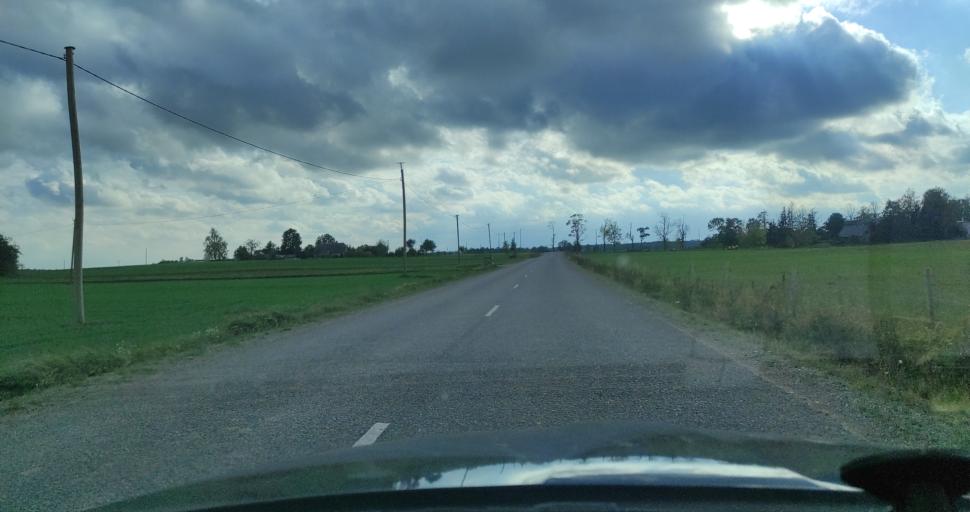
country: LV
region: Talsu Rajons
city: Sabile
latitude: 56.9442
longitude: 22.3980
